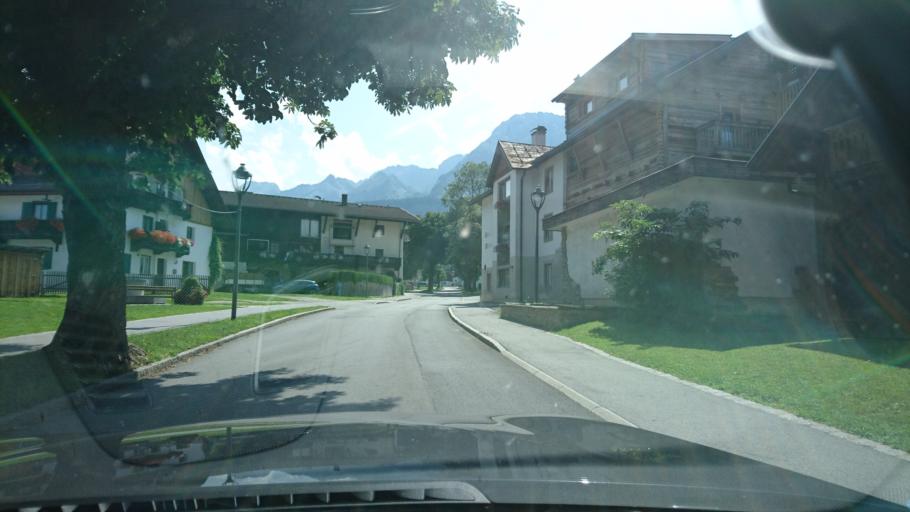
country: AT
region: Tyrol
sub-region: Politischer Bezirk Reutte
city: Ehrwald
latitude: 47.3978
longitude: 10.9210
